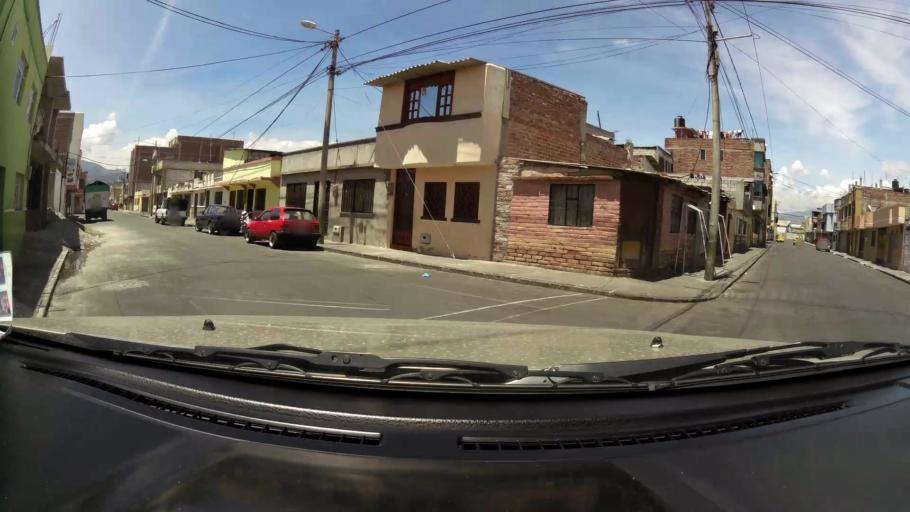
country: EC
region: Chimborazo
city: Riobamba
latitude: -1.6625
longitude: -78.6516
